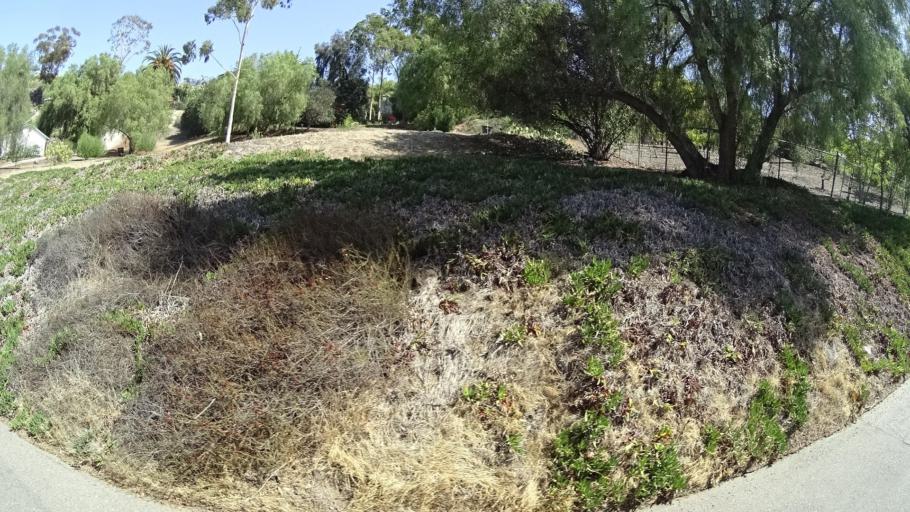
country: US
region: California
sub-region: San Diego County
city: Spring Valley
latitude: 32.7360
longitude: -116.9914
